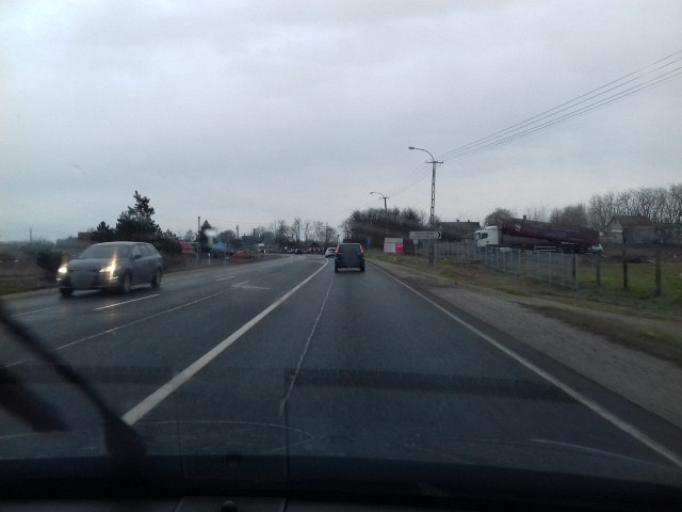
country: HU
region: Szabolcs-Szatmar-Bereg
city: Ujfeherto
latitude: 47.8262
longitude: 21.6990
